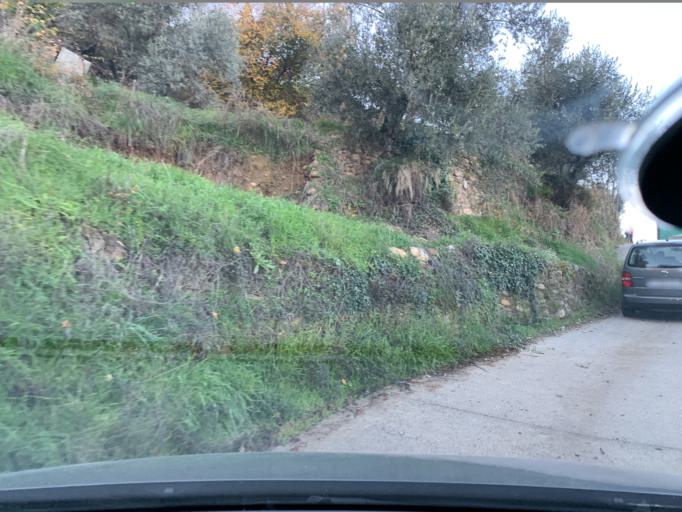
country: ES
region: Andalusia
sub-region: Provincia de Granada
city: Dilar
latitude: 37.0741
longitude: -3.5972
